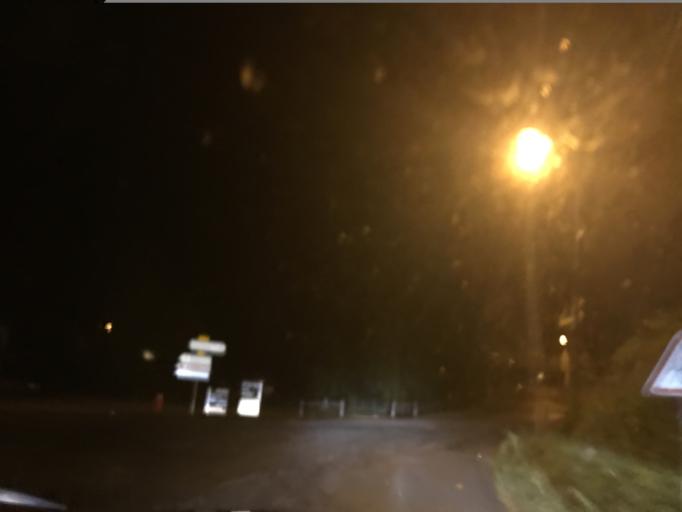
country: FR
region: Auvergne
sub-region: Departement du Puy-de-Dome
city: Celles-sur-Durolle
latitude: 45.7865
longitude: 3.6735
